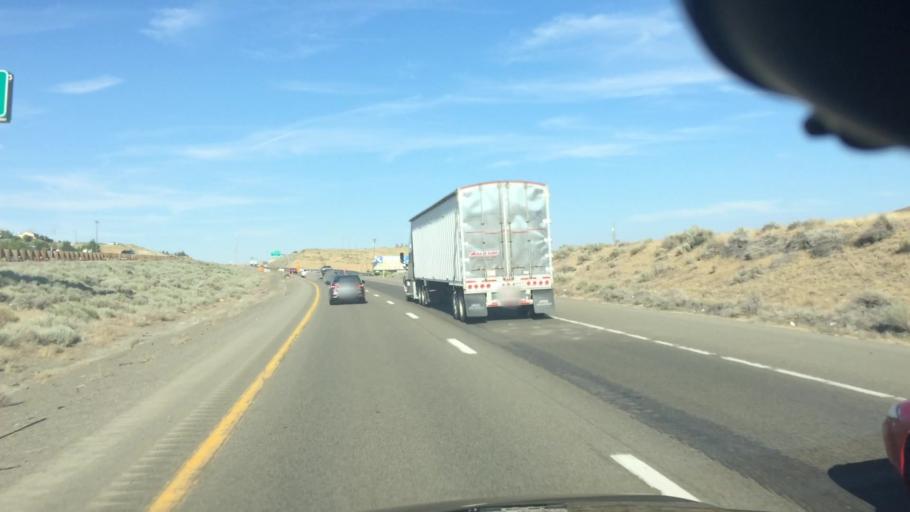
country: US
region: Nevada
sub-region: Washoe County
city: Mogul
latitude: 39.5132
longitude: -119.9040
